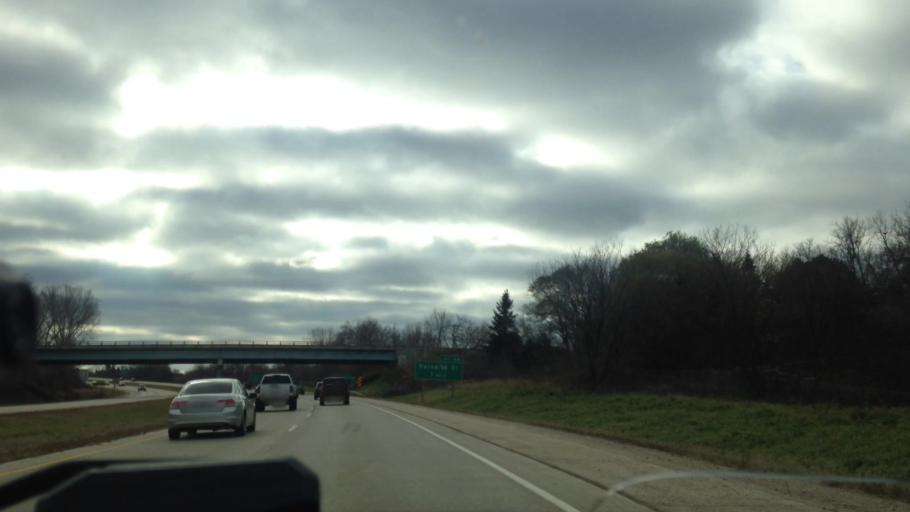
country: US
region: Wisconsin
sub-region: Washington County
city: West Bend
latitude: 43.4142
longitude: -88.2065
